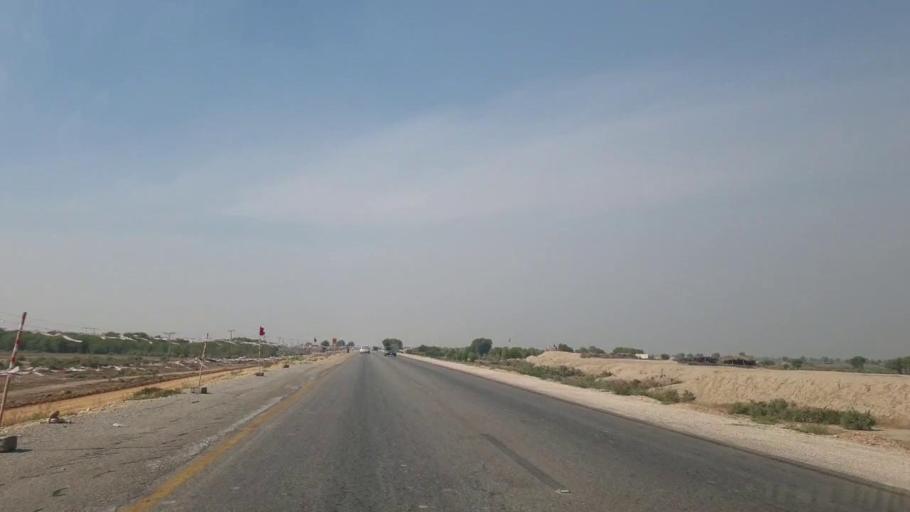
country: PK
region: Sindh
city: Sann
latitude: 25.9939
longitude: 68.1711
